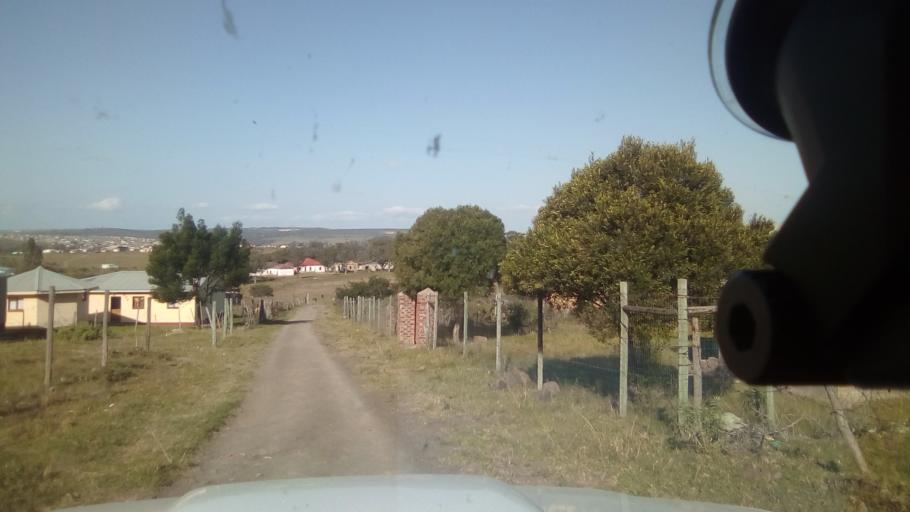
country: ZA
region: Eastern Cape
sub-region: Buffalo City Metropolitan Municipality
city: Bhisho
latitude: -32.8130
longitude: 27.3570
